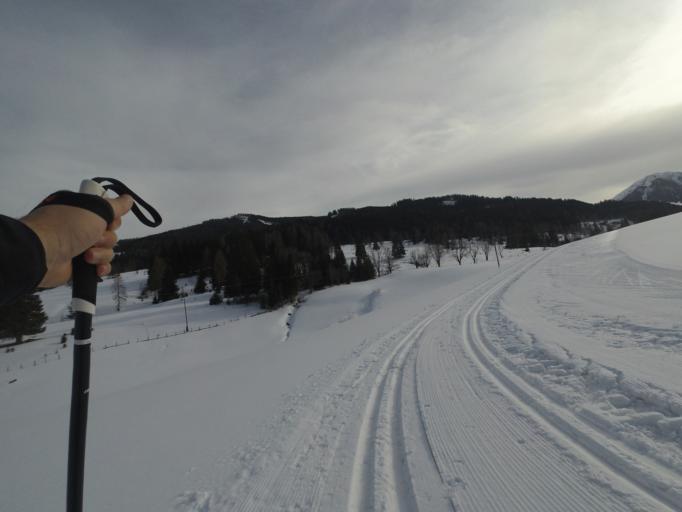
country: AT
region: Salzburg
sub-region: Politischer Bezirk Zell am See
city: Taxenbach
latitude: 47.2877
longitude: 12.9936
